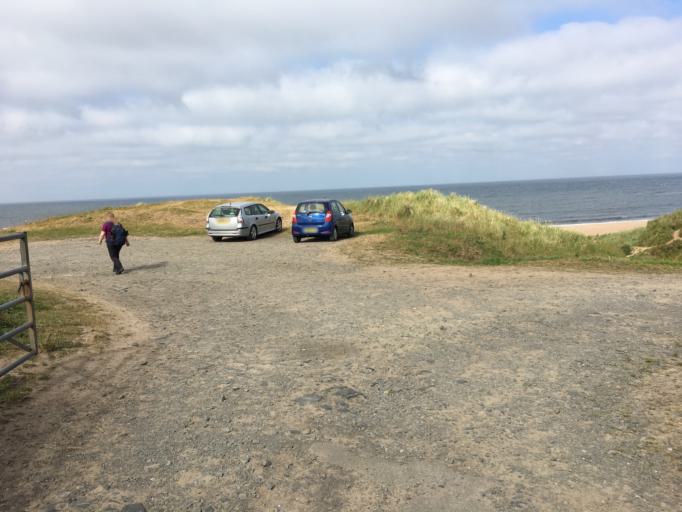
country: GB
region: England
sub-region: Northumberland
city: Alnmouth
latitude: 55.4339
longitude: -1.5884
